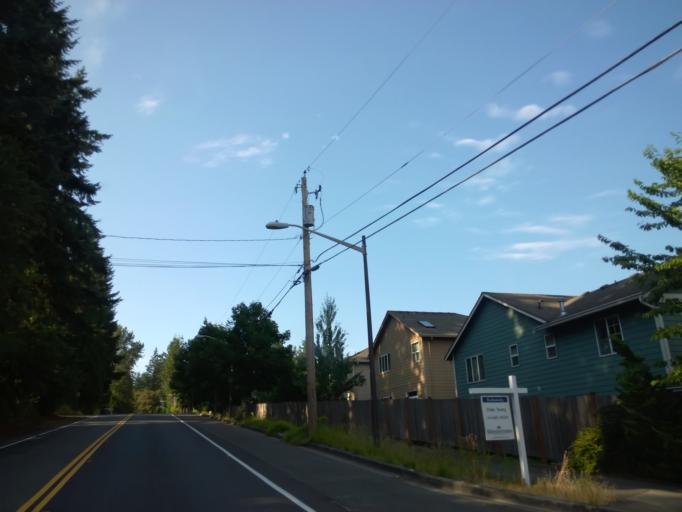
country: US
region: Washington
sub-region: King County
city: Woodinville
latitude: 47.7741
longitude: -122.1586
